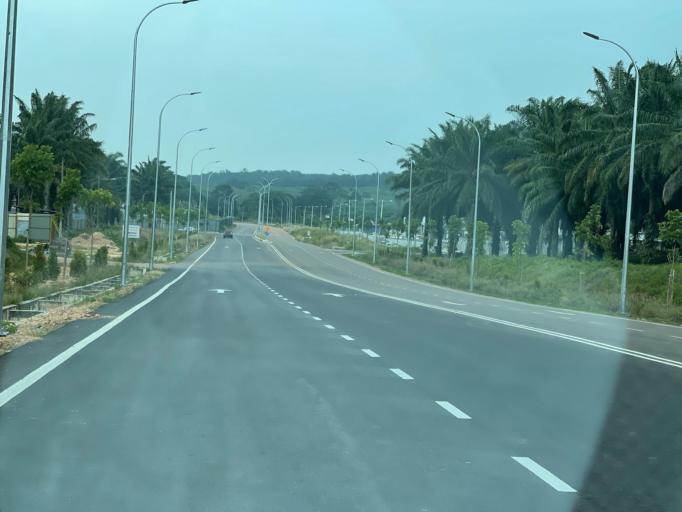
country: MY
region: Melaka
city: Kampung Ayer Keroh
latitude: 2.3181
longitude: 102.2471
